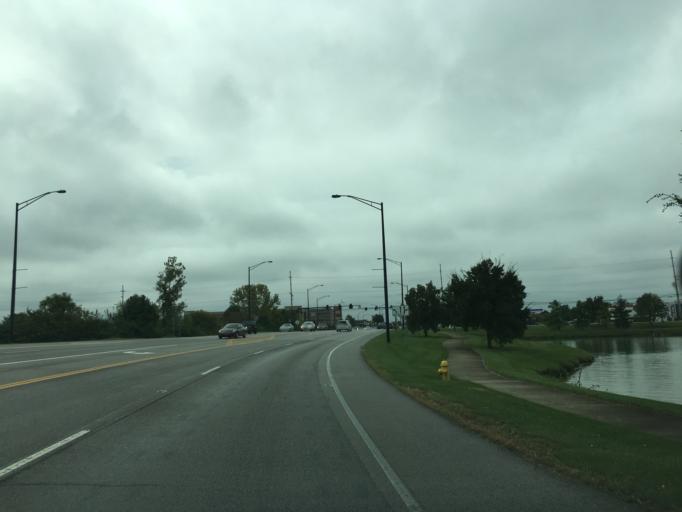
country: US
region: Ohio
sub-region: Butler County
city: Beckett Ridge
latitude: 39.3313
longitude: -84.4352
